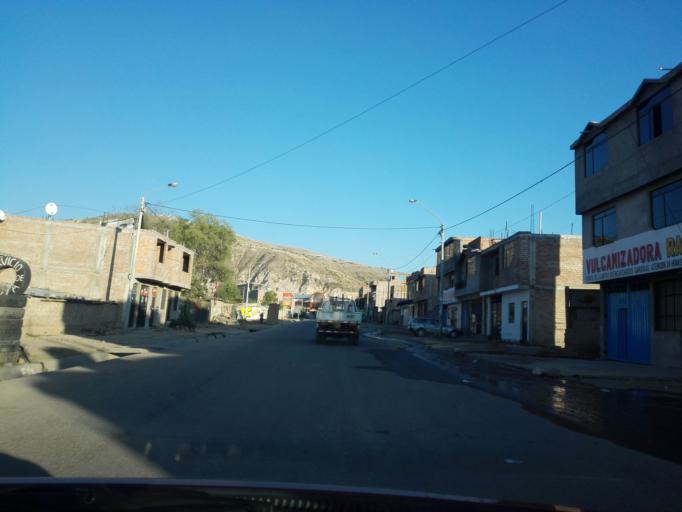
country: PE
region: Ayacucho
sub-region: Provincia de Huamanga
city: Ayacucho
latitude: -13.1354
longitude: -74.2275
